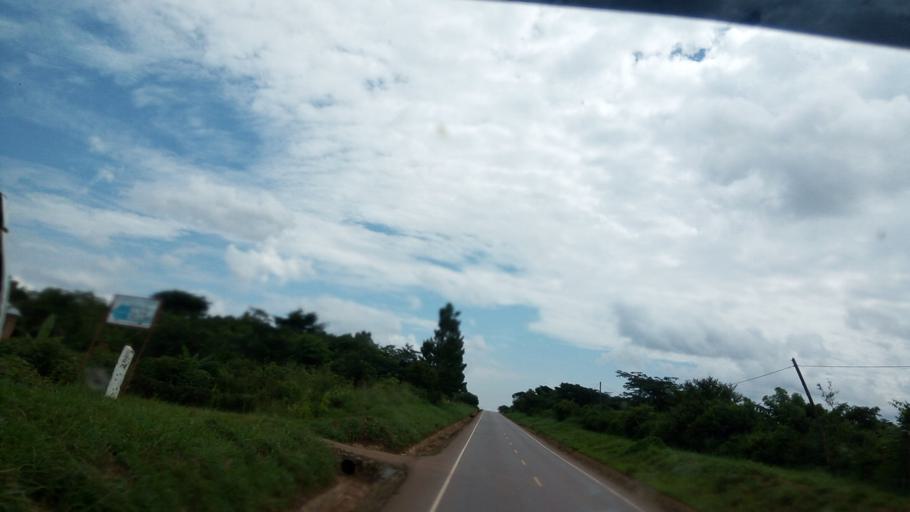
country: UG
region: Central Region
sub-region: Nakasongola District
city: Nakasongola
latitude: 1.1195
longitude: 32.4656
